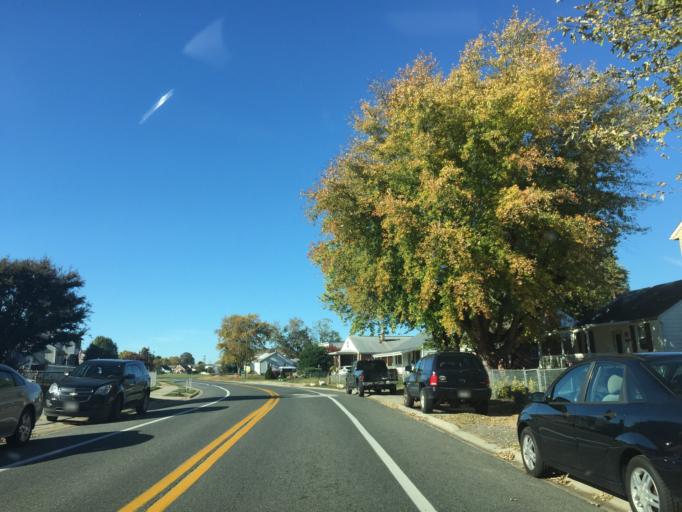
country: US
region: Maryland
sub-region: Baltimore County
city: Dundalk
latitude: 39.2742
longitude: -76.4947
